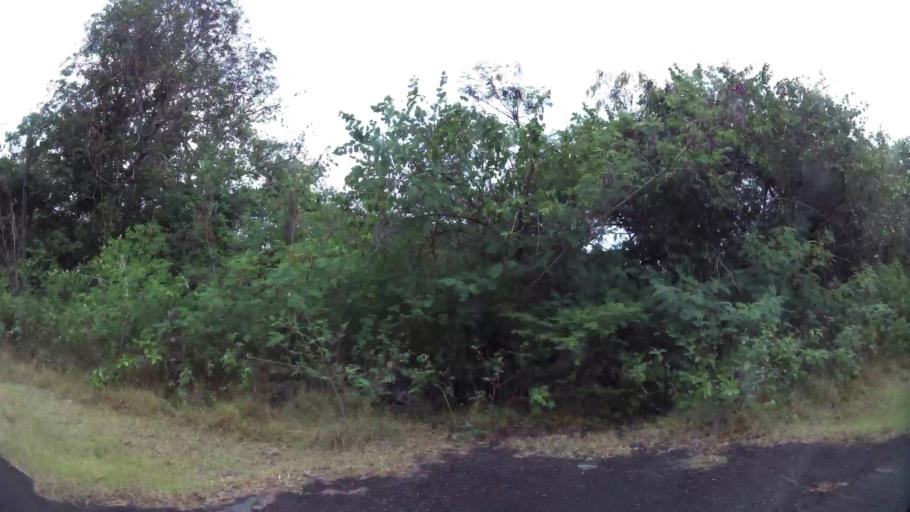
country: KN
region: Saint James Windwa
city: Newcastle
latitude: 17.2023
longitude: -62.6006
